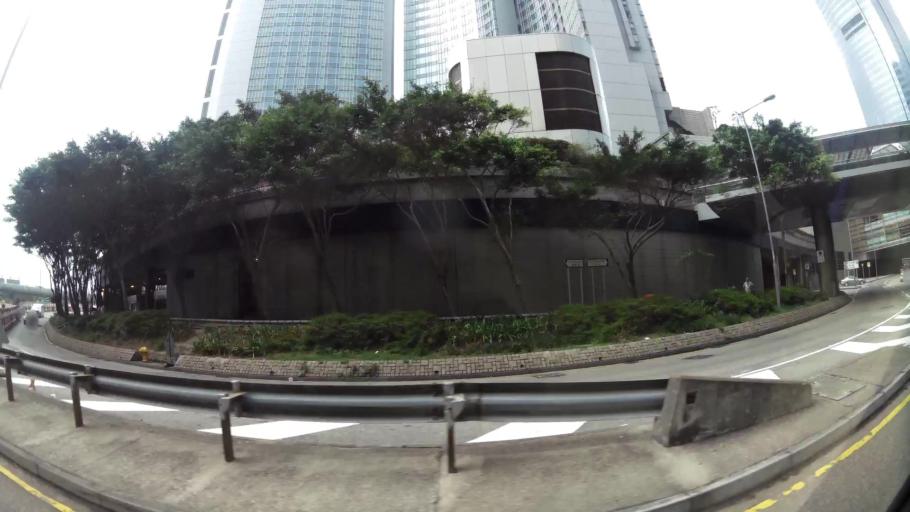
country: HK
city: Hong Kong
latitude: 22.2867
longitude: 114.1560
